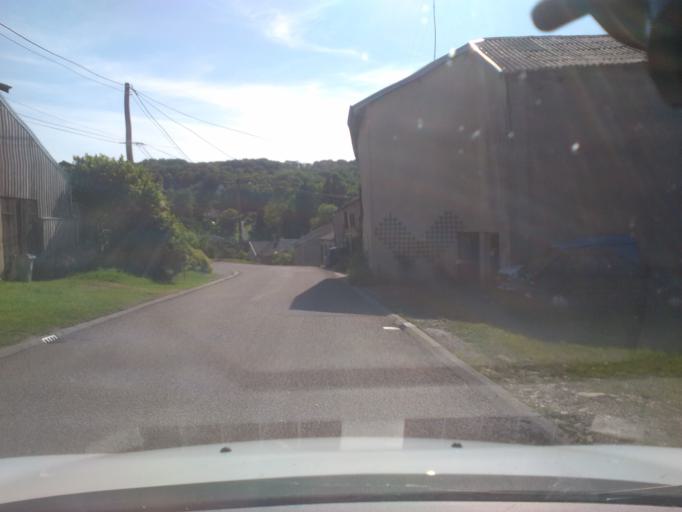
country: FR
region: Lorraine
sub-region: Departement des Vosges
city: Mirecourt
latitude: 48.3398
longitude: 6.1940
